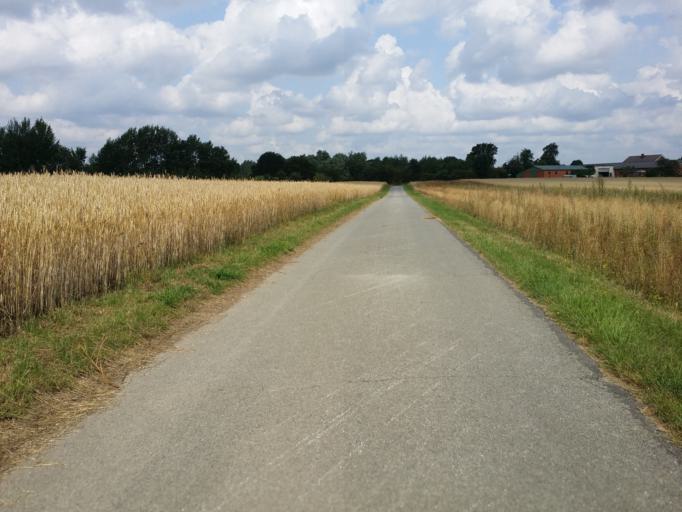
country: DE
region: Schleswig-Holstein
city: Mehlbek
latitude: 53.9992
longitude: 9.4276
